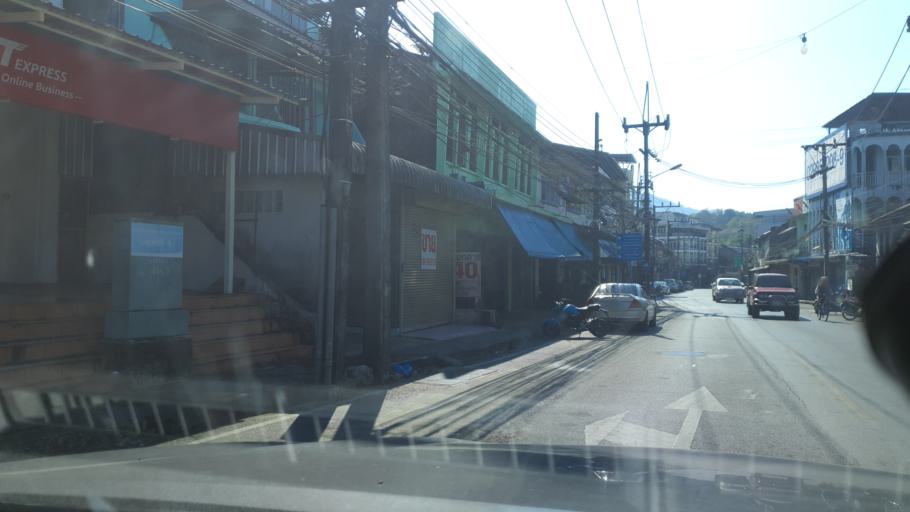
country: TH
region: Ranong
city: Ranong
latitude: 9.9656
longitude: 98.6336
